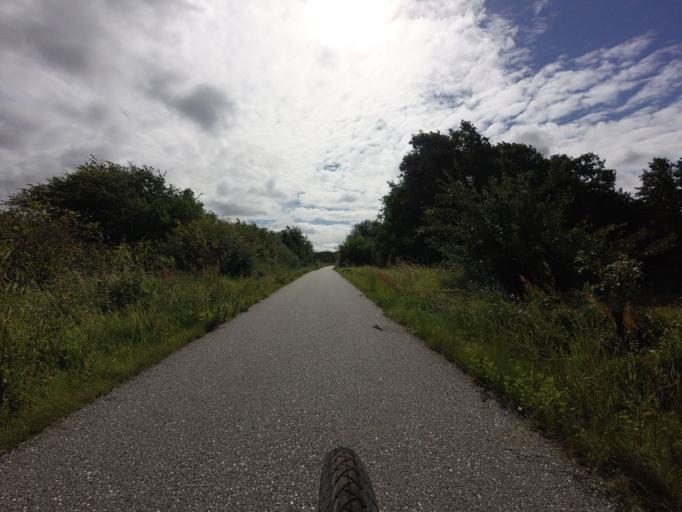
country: DK
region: Central Jutland
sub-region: Norddjurs Kommune
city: Auning
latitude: 56.4507
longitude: 10.3589
